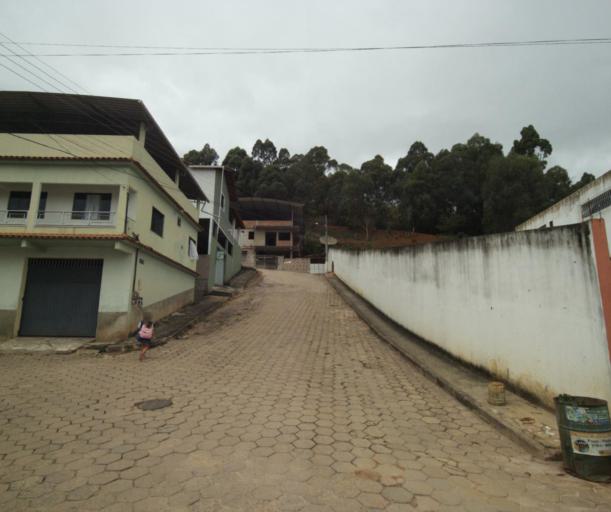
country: BR
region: Espirito Santo
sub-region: Irupi
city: Irupi
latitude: -20.3476
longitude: -41.6432
